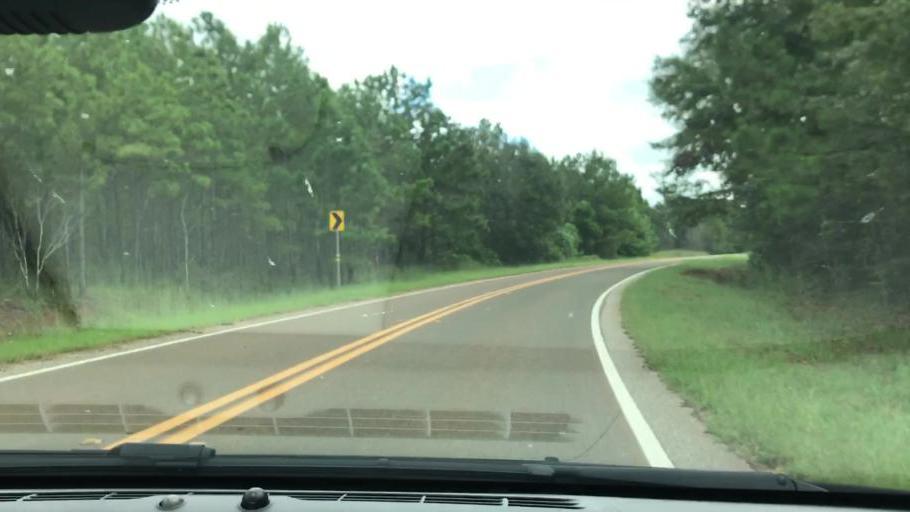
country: US
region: Georgia
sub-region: Stewart County
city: Lumpkin
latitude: 32.0728
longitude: -84.8765
